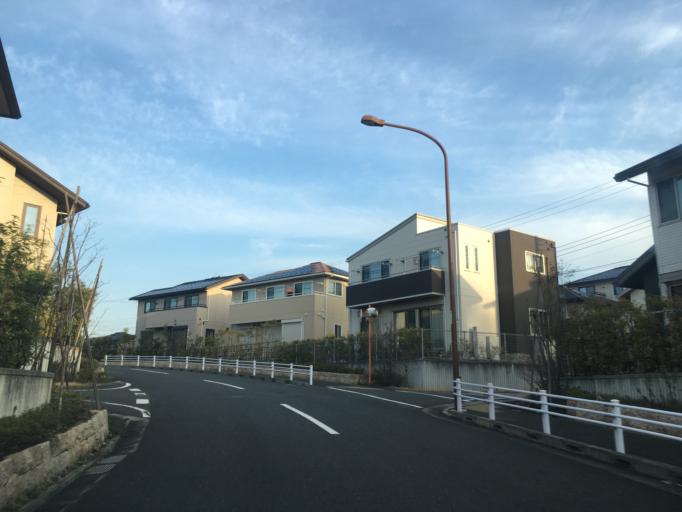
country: JP
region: Tokyo
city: Hino
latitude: 35.6337
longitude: 139.4001
